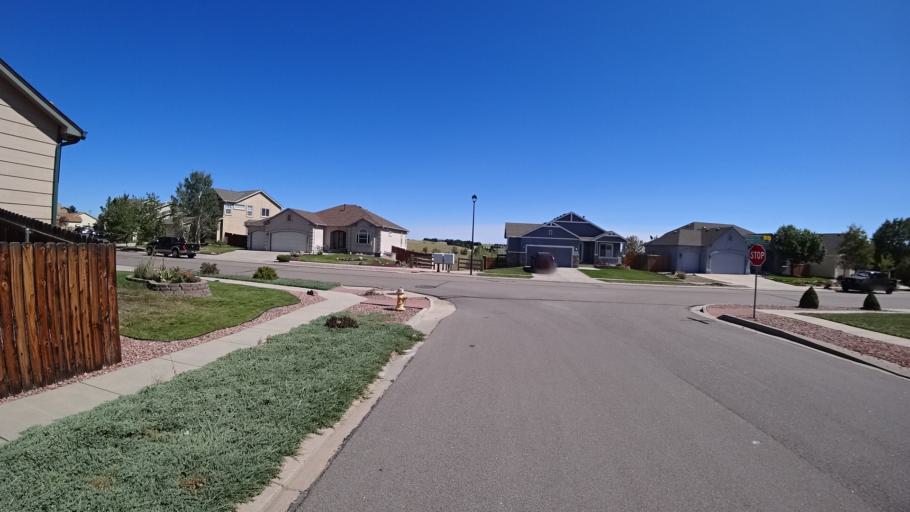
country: US
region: Colorado
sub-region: El Paso County
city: Security-Widefield
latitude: 38.7829
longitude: -104.7273
